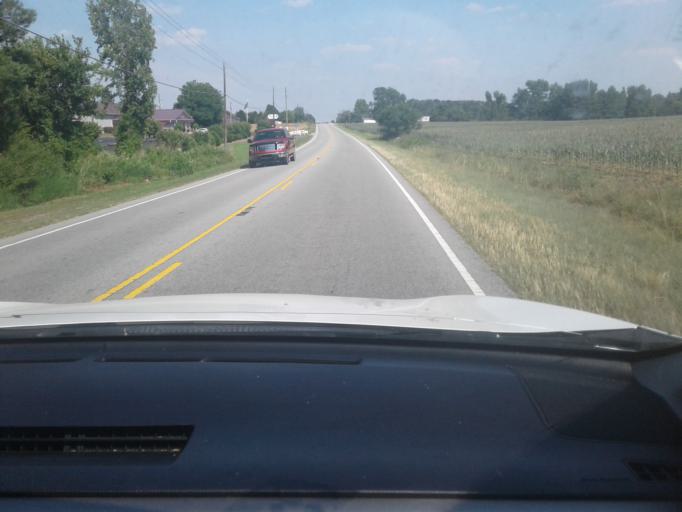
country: US
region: North Carolina
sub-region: Johnston County
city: Benson
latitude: 35.3953
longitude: -78.5944
